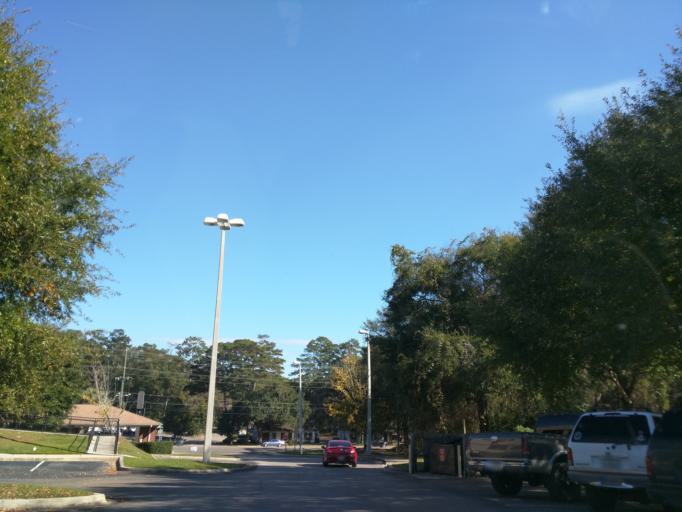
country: US
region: Florida
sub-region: Leon County
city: Tallahassee
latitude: 30.4622
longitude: -84.2829
